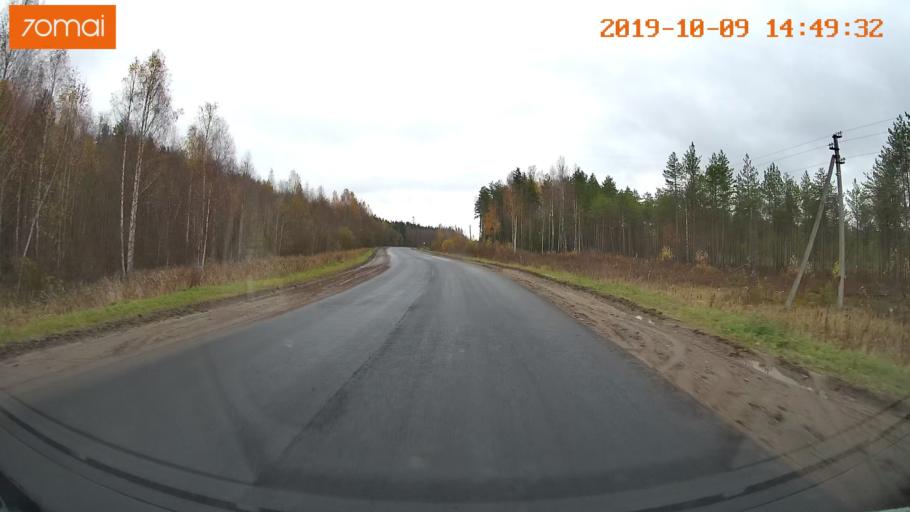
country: RU
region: Kostroma
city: Chistyye Bory
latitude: 58.3924
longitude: 41.5833
